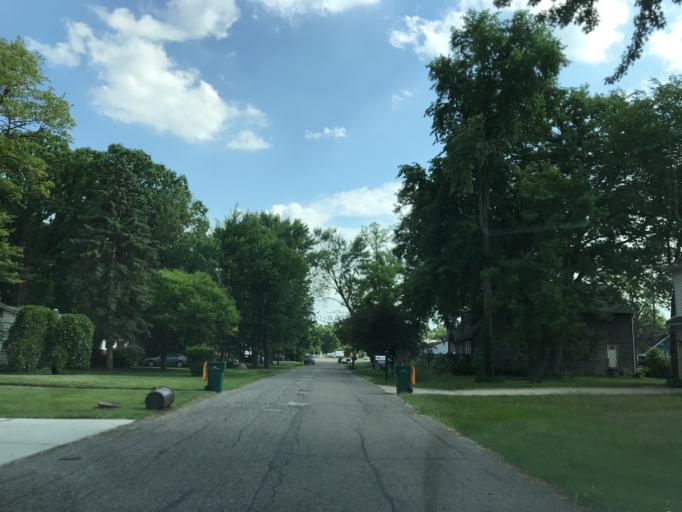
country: US
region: Michigan
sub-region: Oakland County
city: Farmington
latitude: 42.4483
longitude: -83.3317
